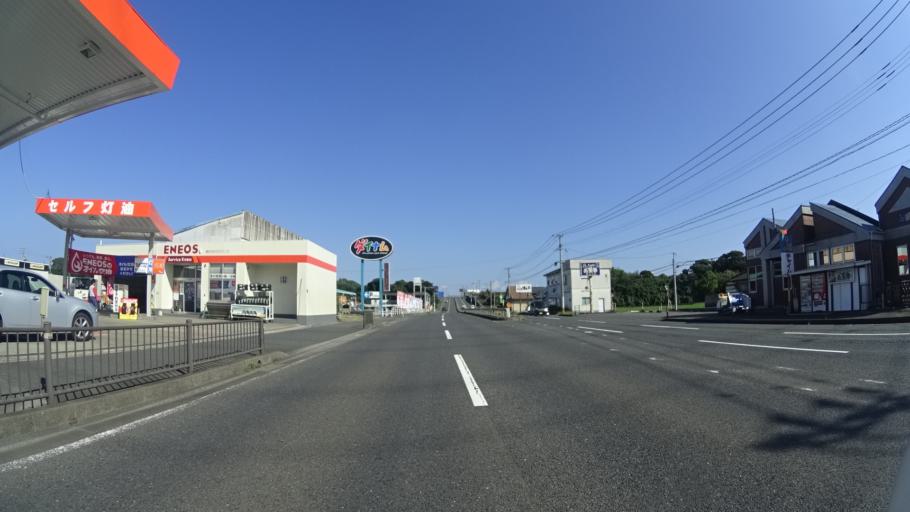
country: JP
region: Fukuoka
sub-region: Buzen-shi
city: Buzen
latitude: 33.6098
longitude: 131.1101
